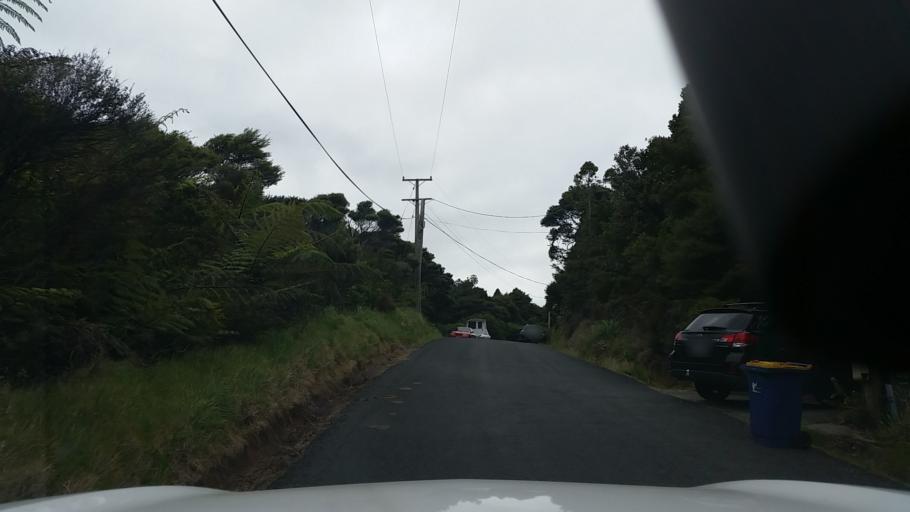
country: NZ
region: Auckland
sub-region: Auckland
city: Muriwai Beach
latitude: -36.8758
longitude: 174.4787
